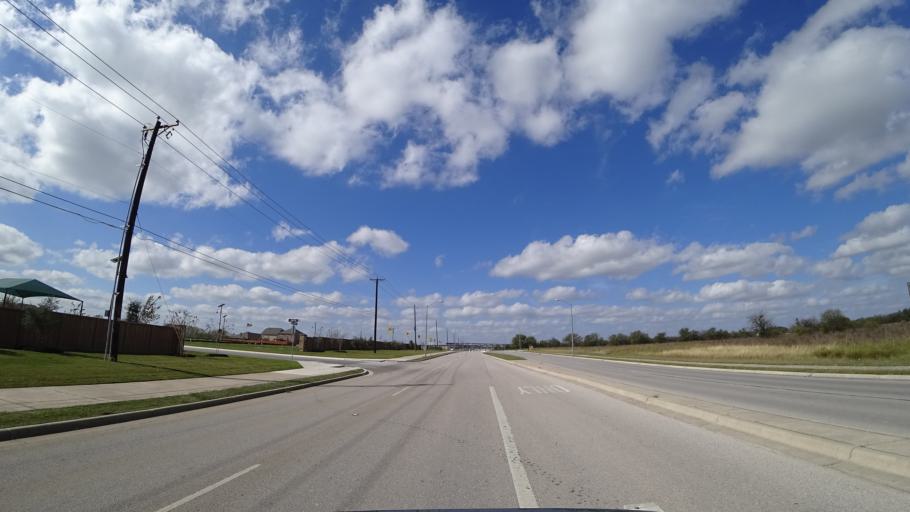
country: US
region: Texas
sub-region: Travis County
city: Windemere
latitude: 30.4736
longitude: -97.6559
